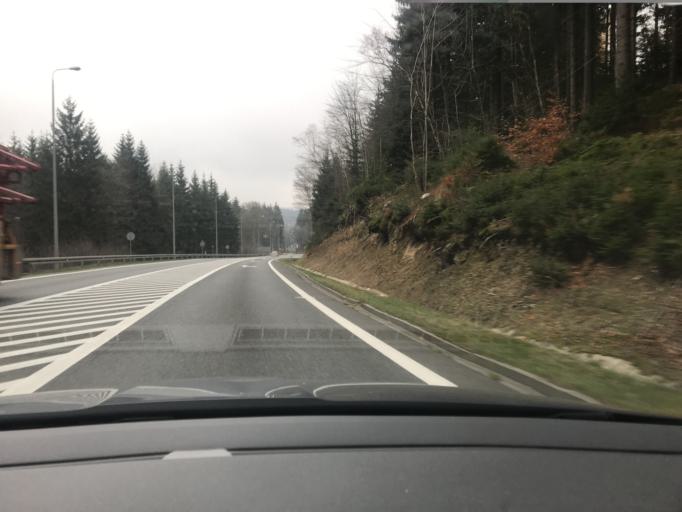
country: PL
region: Lower Silesian Voivodeship
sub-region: Powiat klodzki
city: Duszniki-Zdroj
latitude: 50.3975
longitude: 16.3509
